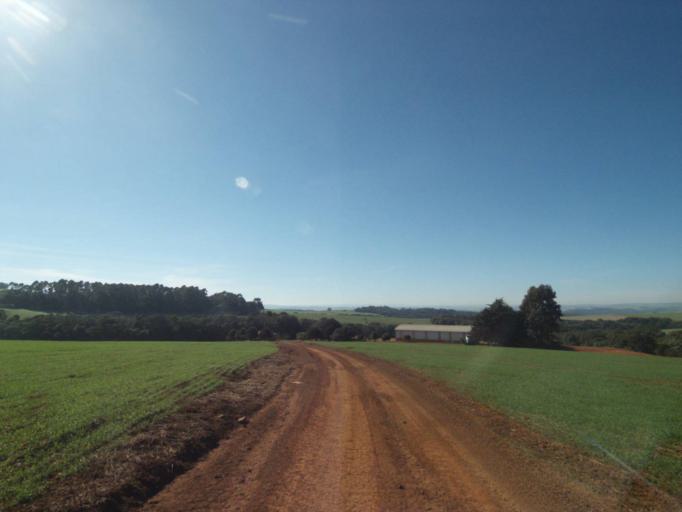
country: BR
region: Parana
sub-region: Tibagi
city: Tibagi
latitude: -24.3893
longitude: -50.3279
